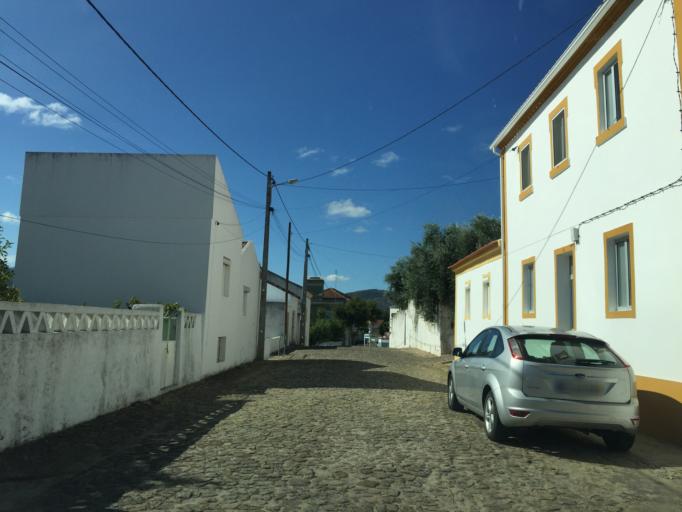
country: PT
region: Portalegre
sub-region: Marvao
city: Marvao
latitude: 39.4485
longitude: -7.3705
